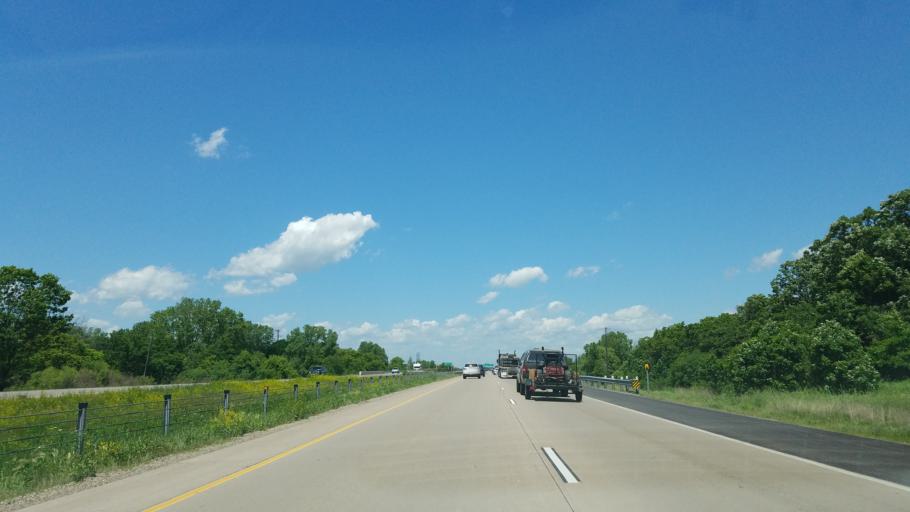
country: US
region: Minnesota
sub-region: Ramsey County
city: North Saint Paul
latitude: 45.0191
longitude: -92.9590
